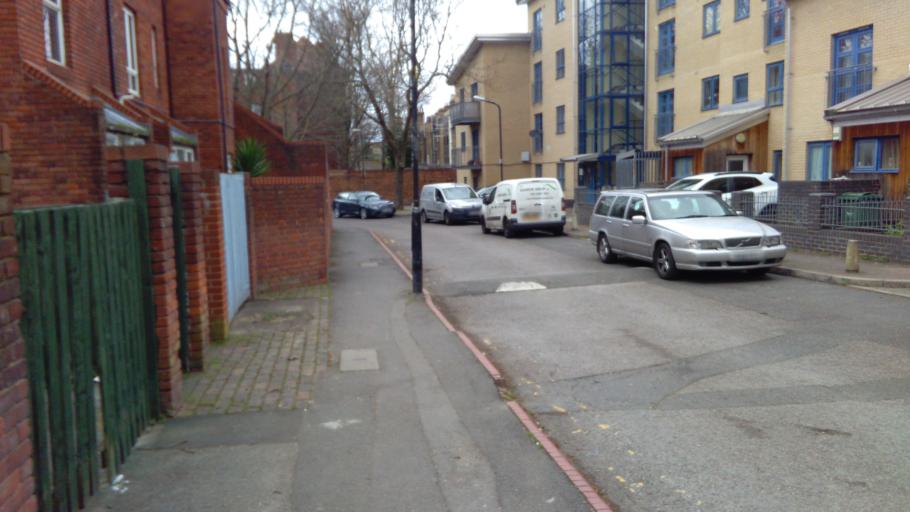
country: GB
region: England
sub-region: Greater London
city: Brixton Hill
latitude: 51.4609
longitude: -0.1312
